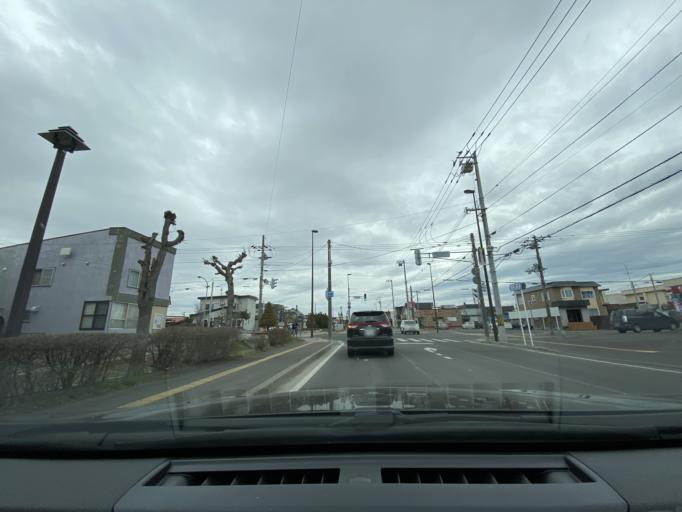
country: JP
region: Hokkaido
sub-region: Asahikawa-shi
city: Asahikawa
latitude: 43.7927
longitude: 142.4172
